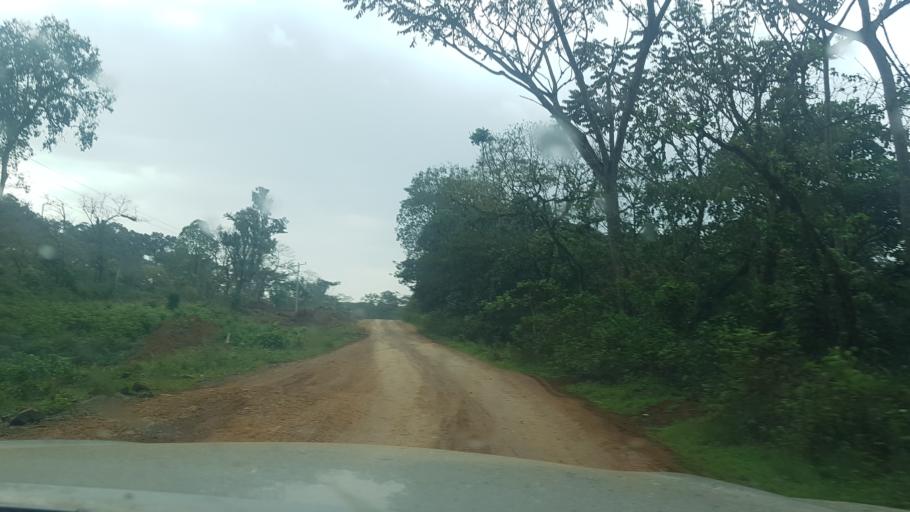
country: ET
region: Oromiya
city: Gore
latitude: 7.8858
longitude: 35.4860
